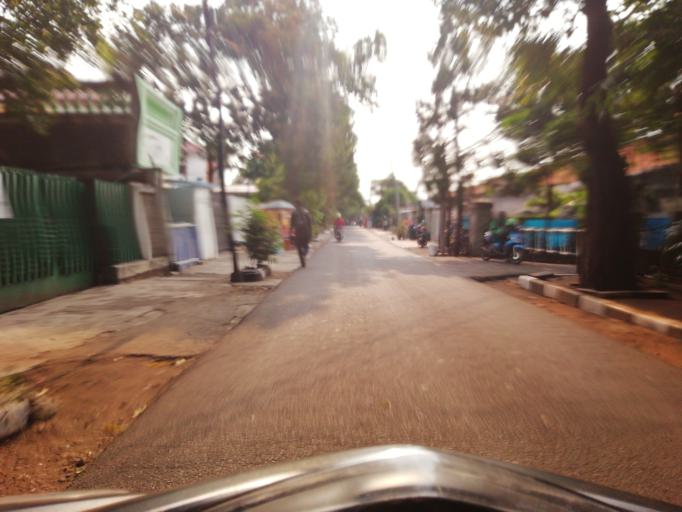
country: ID
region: West Java
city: Pamulang
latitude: -6.3068
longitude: 106.8124
